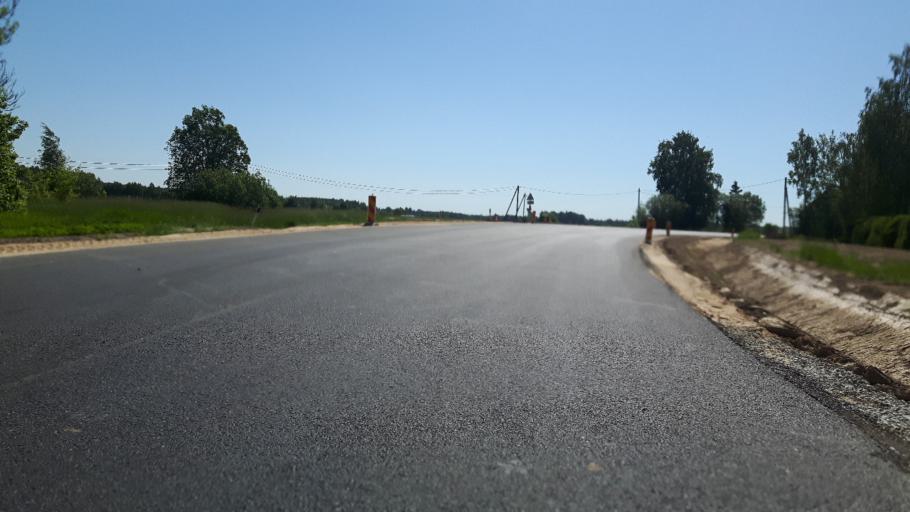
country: EE
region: Paernumaa
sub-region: Sindi linn
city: Sindi
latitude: 58.4199
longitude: 24.7144
